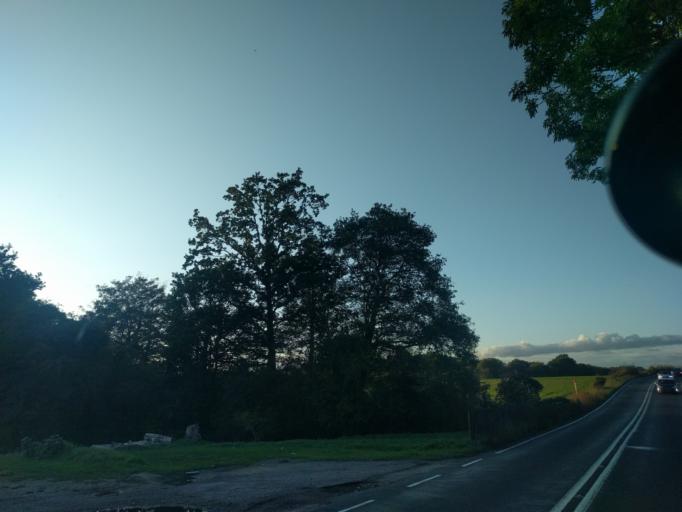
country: GB
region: England
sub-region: Essex
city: Witham
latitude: 51.8193
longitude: 0.6262
